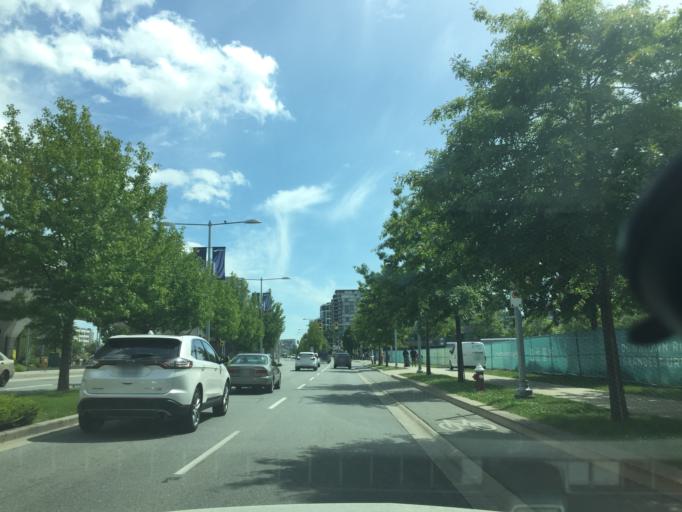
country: CA
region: British Columbia
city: Richmond
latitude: 49.1765
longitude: -123.1368
